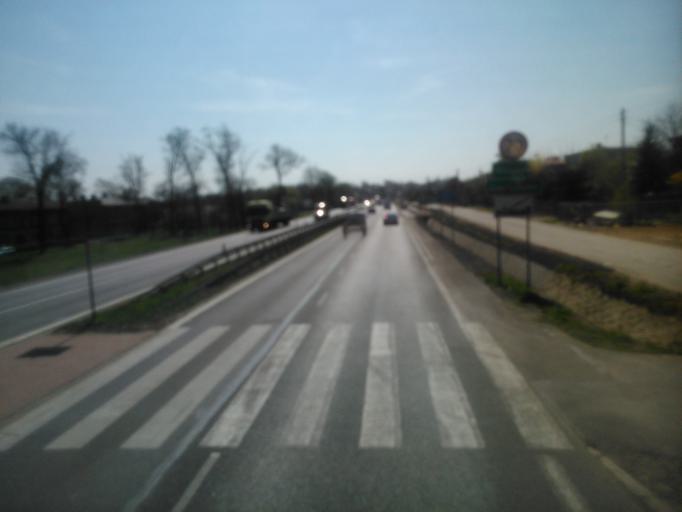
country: PL
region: Silesian Voivodeship
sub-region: Powiat czestochowski
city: Huta Stara B
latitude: 50.7565
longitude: 19.1566
